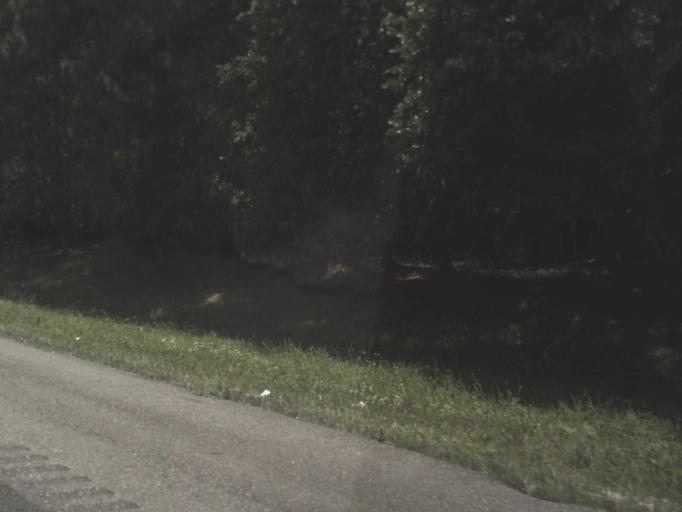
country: US
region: Florida
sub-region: Clay County
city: Bellair-Meadowbrook Terrace
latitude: 30.2760
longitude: -81.7698
